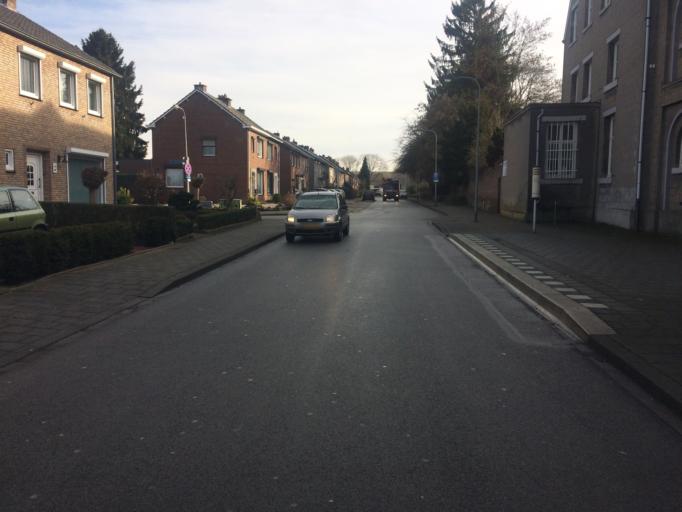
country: NL
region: Limburg
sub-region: Gemeente Maastricht
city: Heer
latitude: 50.8363
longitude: 5.7296
